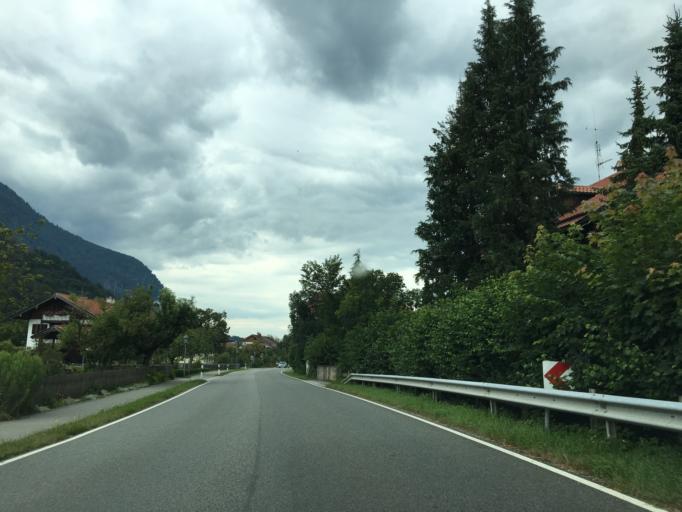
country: DE
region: Bavaria
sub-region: Upper Bavaria
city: Oberaudorf
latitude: 47.6649
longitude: 12.1702
